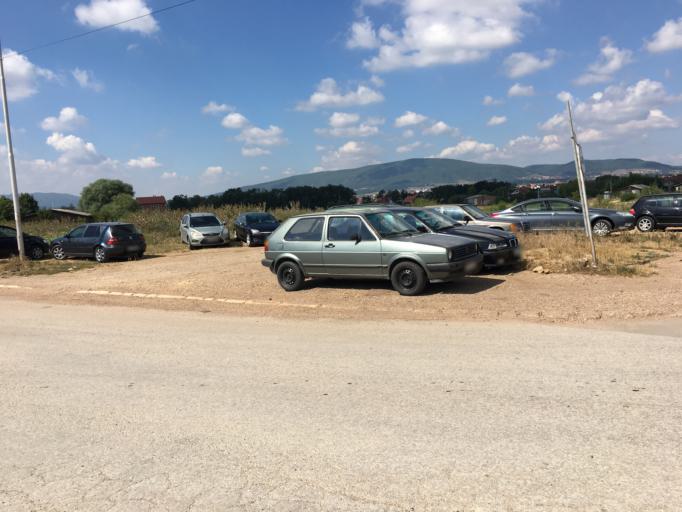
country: XK
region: Pristina
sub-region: Komuna e Drenasit
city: Glogovac
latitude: 42.6384
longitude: 20.9076
